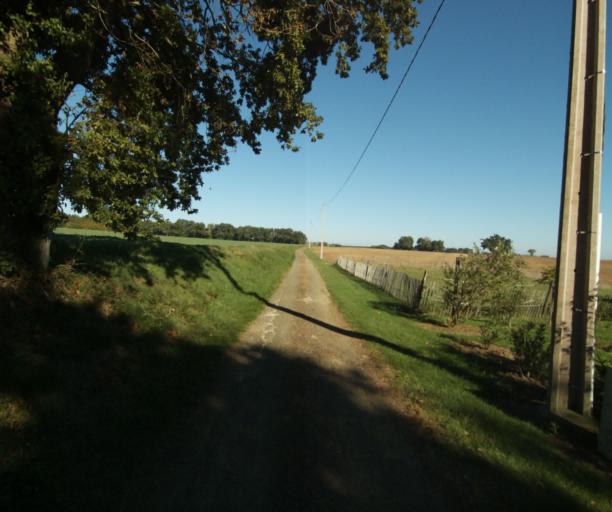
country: FR
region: Midi-Pyrenees
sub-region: Departement du Gers
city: Vic-Fezensac
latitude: 43.8175
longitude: 0.2701
